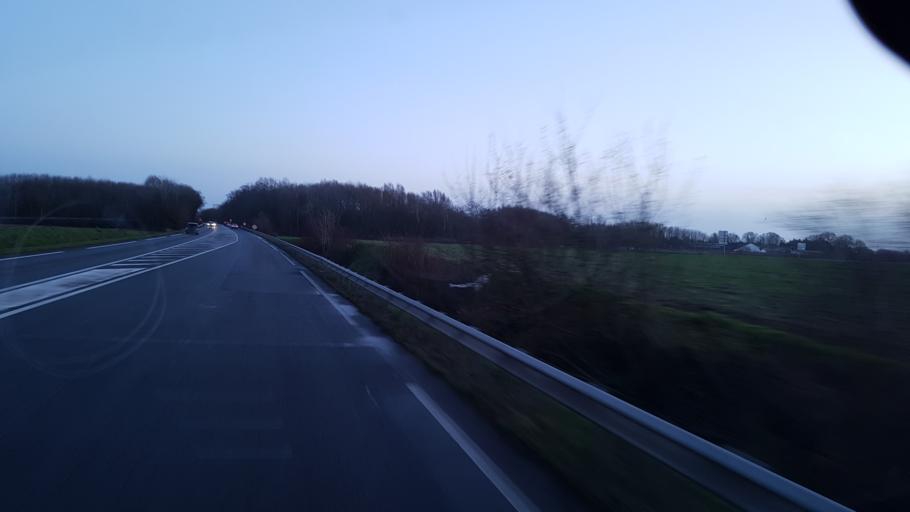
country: FR
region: Nord-Pas-de-Calais
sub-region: Departement du Nord
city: Cuincy
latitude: 50.3597
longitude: 3.0429
